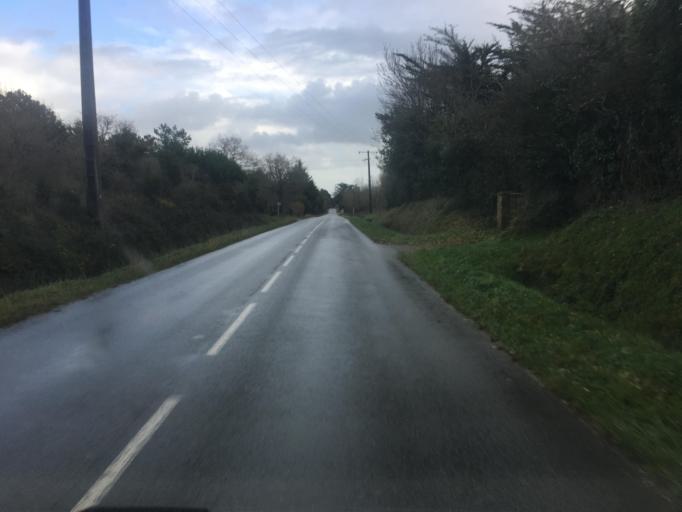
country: FR
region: Brittany
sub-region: Departement du Morbihan
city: Surzur
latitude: 47.5188
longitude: -2.6785
